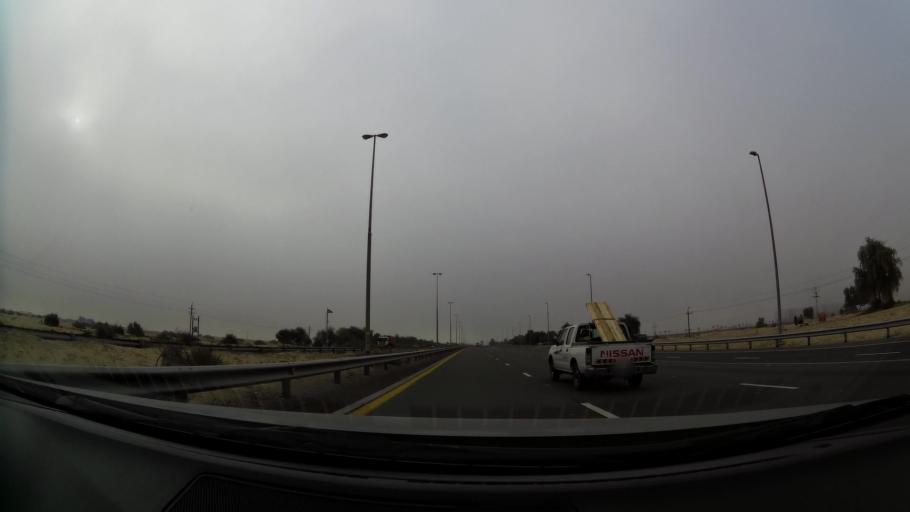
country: AE
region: Dubai
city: Dubai
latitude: 25.0548
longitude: 55.4218
